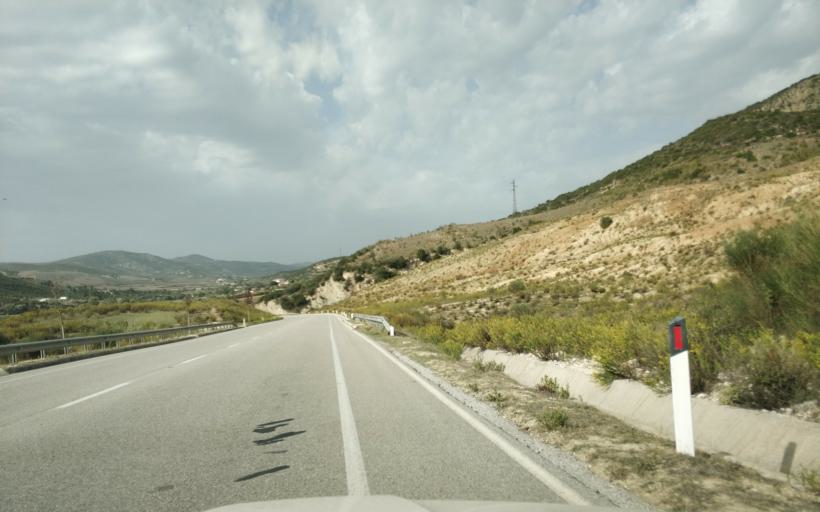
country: AL
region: Gjirokaster
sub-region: Rrethi i Tepelenes
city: Krahes
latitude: 40.4010
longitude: 19.8637
